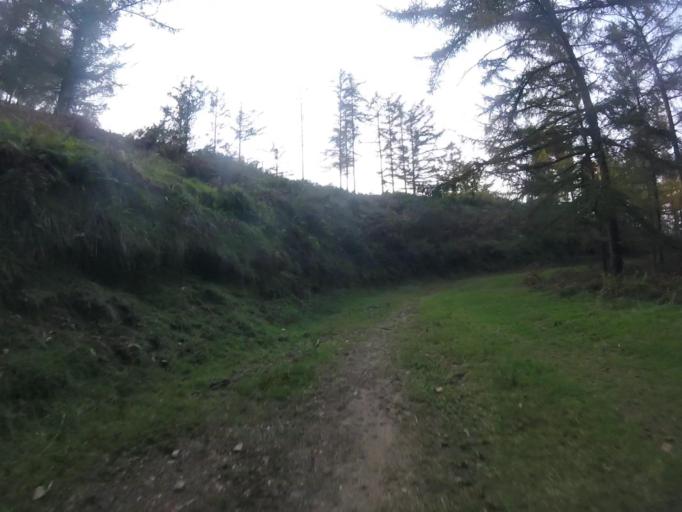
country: ES
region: Navarre
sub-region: Provincia de Navarra
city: Arano
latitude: 43.2573
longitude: -1.8378
